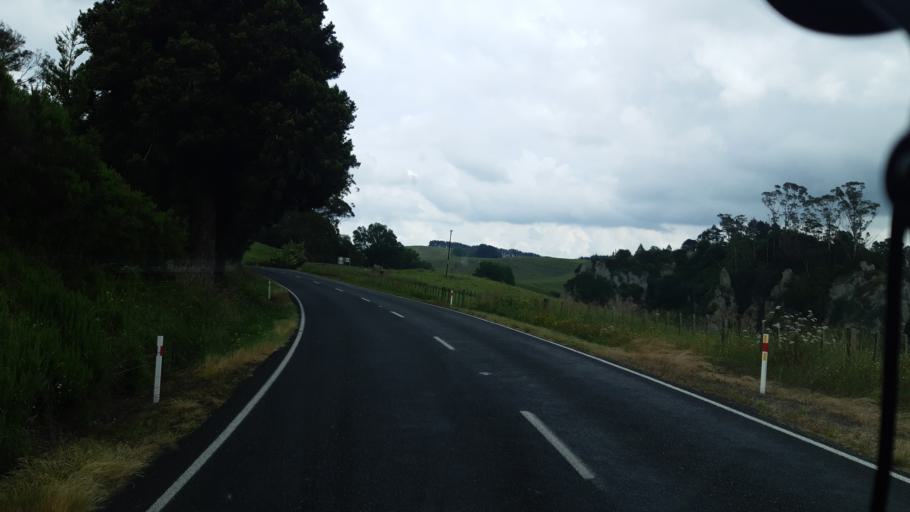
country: NZ
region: Waikato
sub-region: Waipa District
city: Cambridge
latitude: -38.1326
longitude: 175.5256
